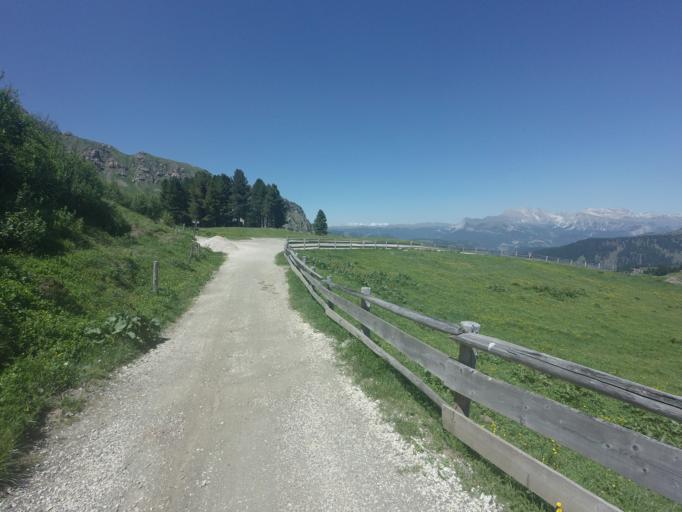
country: IT
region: Trentino-Alto Adige
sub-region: Provincia di Trento
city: Mazzin
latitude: 46.4998
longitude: 11.6512
